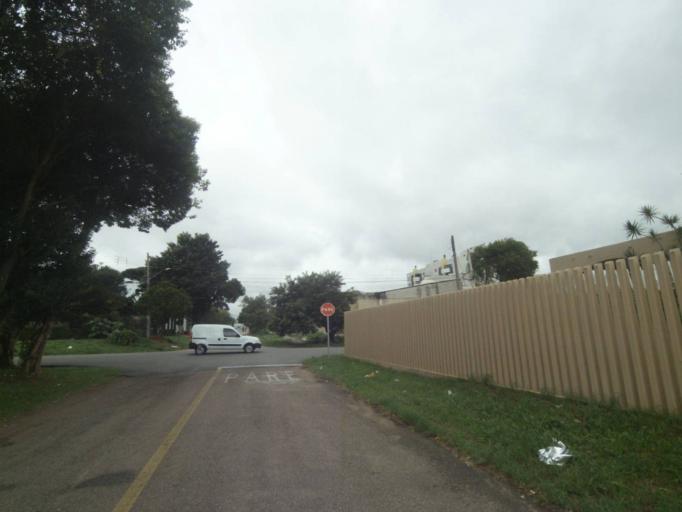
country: BR
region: Parana
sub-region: Curitiba
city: Curitiba
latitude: -25.4935
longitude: -49.2999
